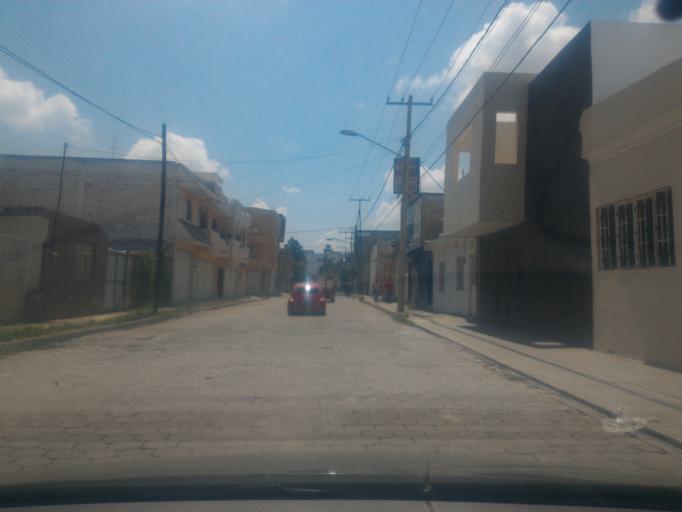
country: MX
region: Guanajuato
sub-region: Purisima del Rincon
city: Monte Grande
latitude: 21.0085
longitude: -101.8614
